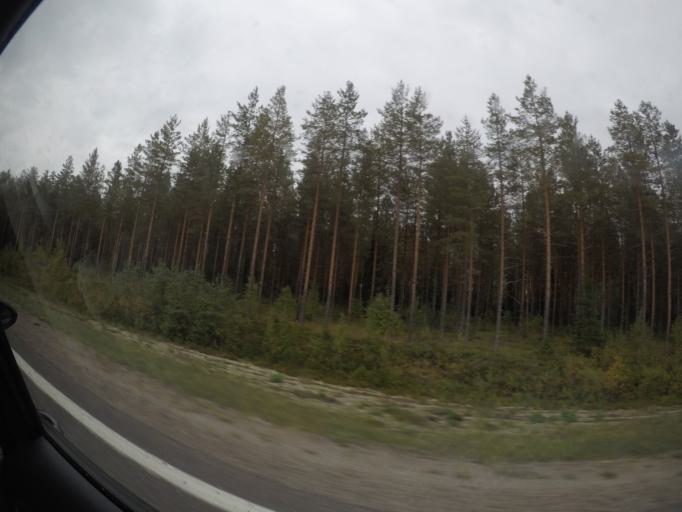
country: FI
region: Pirkanmaa
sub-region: Ylae-Pirkanmaa
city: Juupajoki
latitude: 61.7472
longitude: 24.3111
